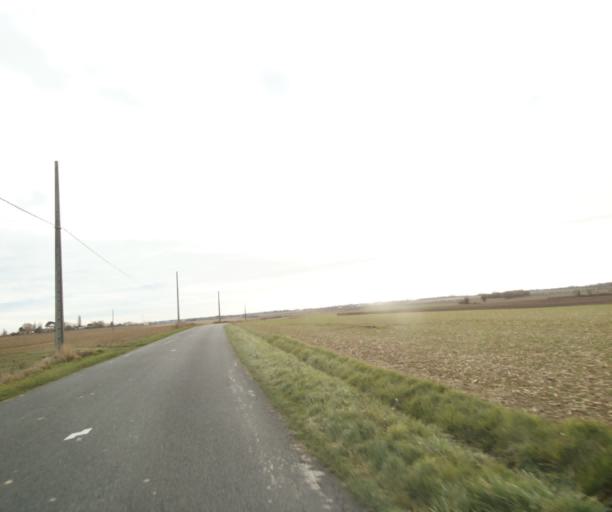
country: FR
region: Poitou-Charentes
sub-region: Departement de la Charente-Maritime
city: Corme-Royal
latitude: 45.7371
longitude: -0.8140
